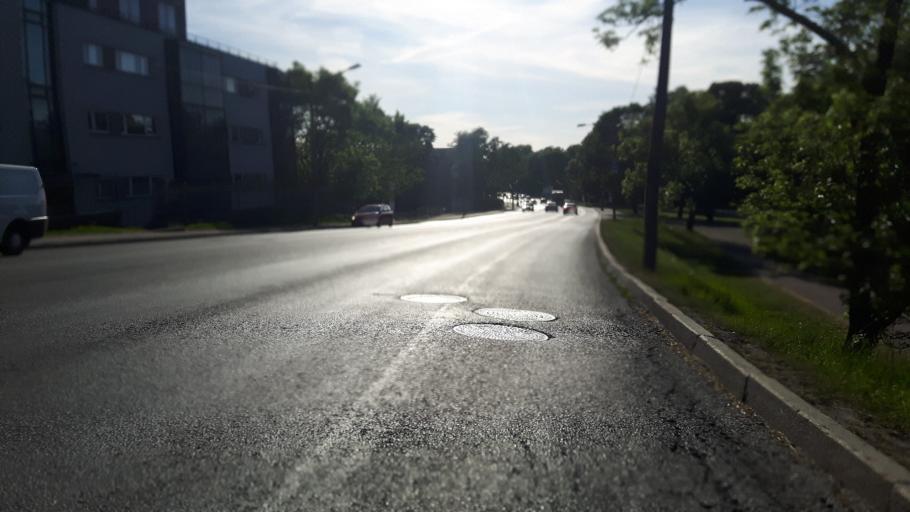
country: EE
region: Harju
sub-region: Tallinna linn
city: Tallinn
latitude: 59.4429
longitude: 24.8078
